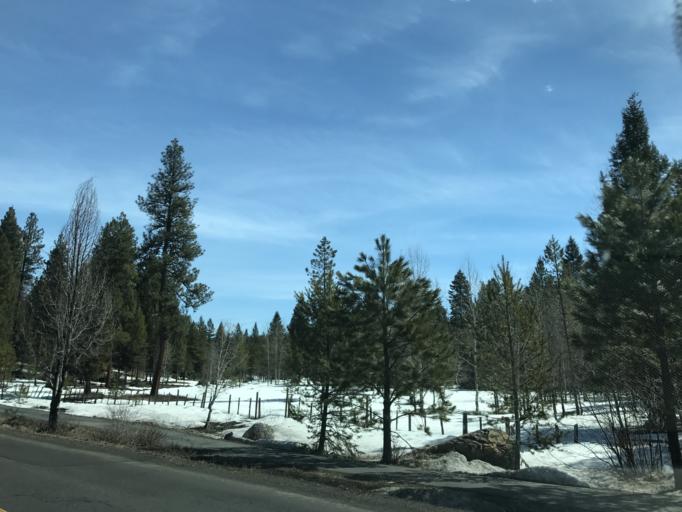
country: US
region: Idaho
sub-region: Valley County
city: McCall
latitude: 44.9082
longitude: -116.0836
